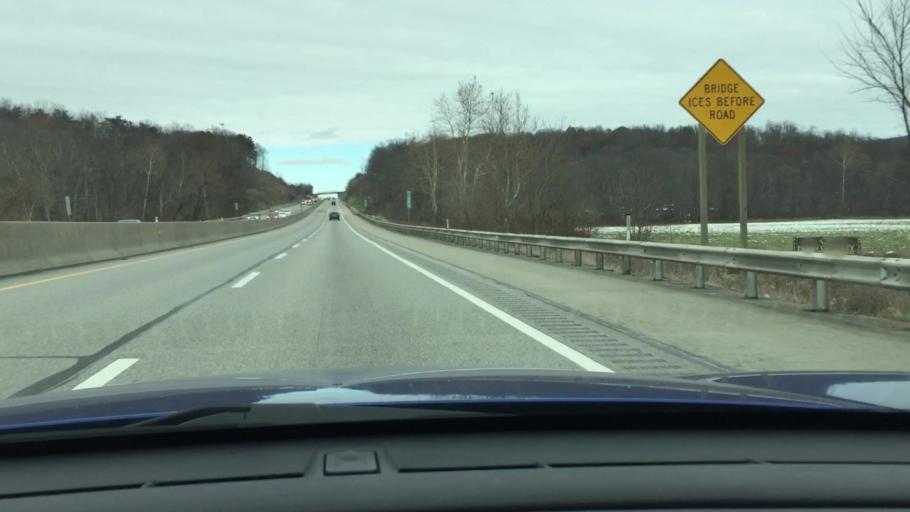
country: US
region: Pennsylvania
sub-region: Bedford County
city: Bedford
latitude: 40.0205
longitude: -78.5842
